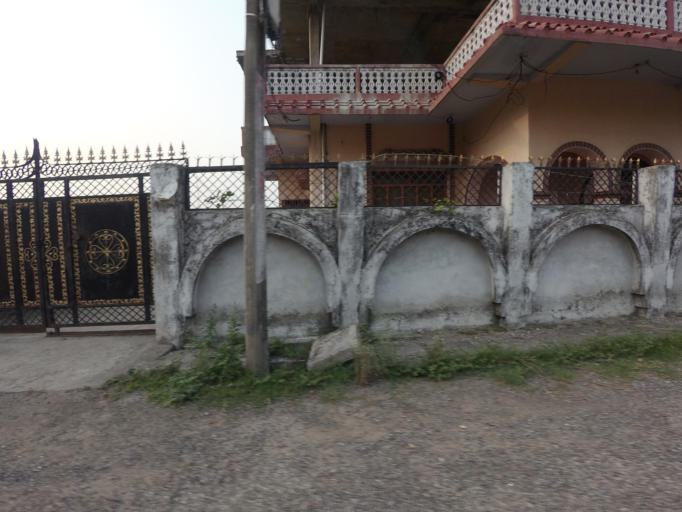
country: NP
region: Western Region
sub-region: Lumbini Zone
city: Bhairahawa
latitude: 27.5158
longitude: 83.4582
